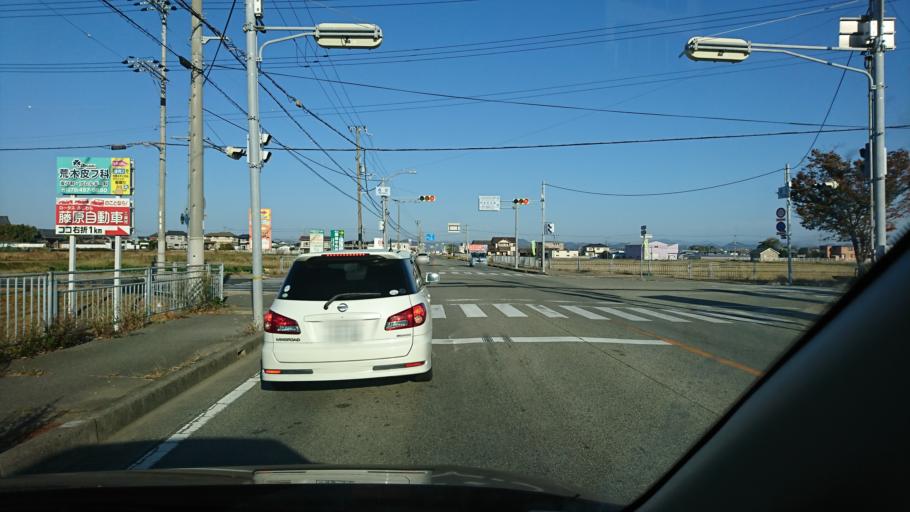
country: JP
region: Hyogo
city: Kakogawacho-honmachi
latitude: 34.7441
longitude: 134.8997
